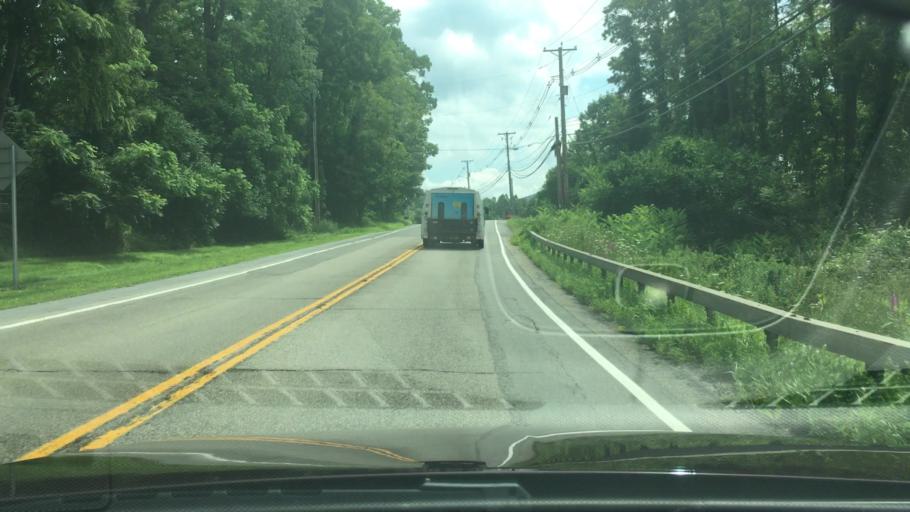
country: US
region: New York
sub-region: Dutchess County
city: Hillside Lake
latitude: 41.5536
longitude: -73.7932
